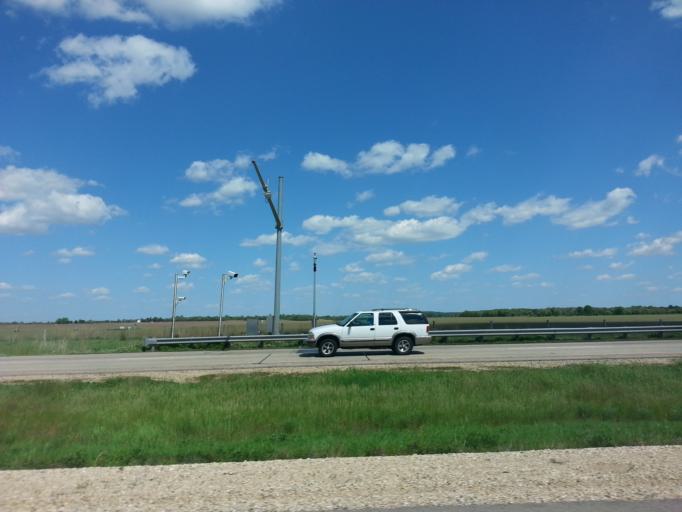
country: US
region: Wisconsin
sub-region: Rock County
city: Beloit
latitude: 42.5786
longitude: -88.9816
